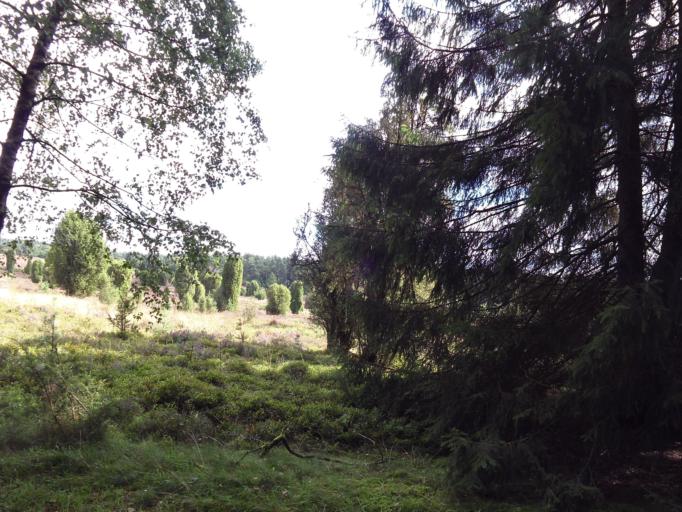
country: DE
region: Lower Saxony
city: Undeloh
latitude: 53.1478
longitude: 9.9559
